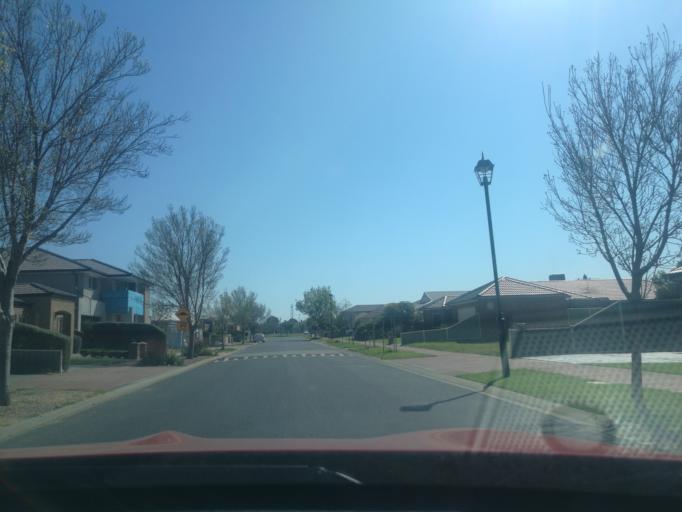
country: AU
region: Victoria
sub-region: Wyndham
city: Point Cook
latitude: -37.8899
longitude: 144.7462
